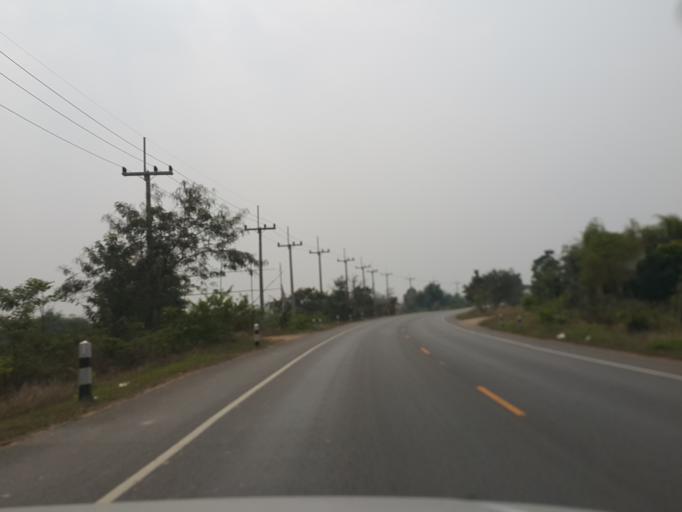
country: TH
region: Lampang
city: Ko Kha
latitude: 18.2213
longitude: 99.3965
